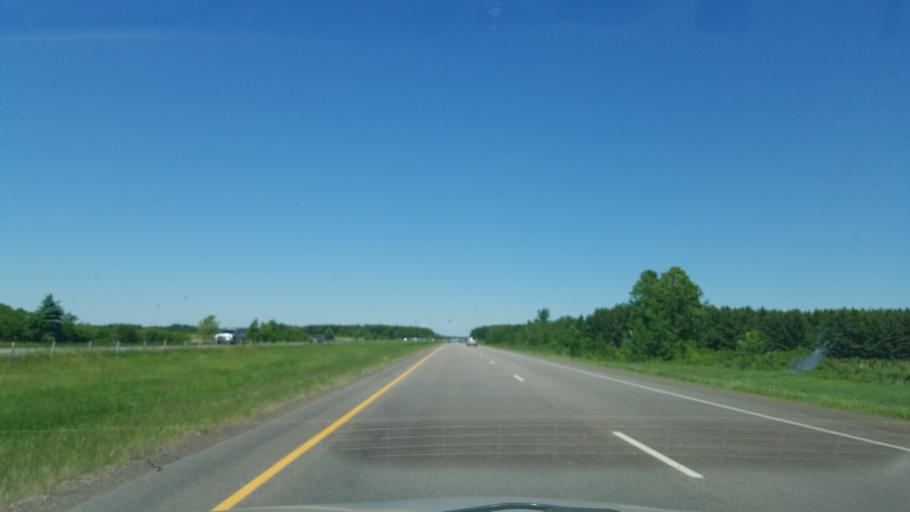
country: US
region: Minnesota
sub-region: Chisago County
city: Rush City
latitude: 45.7065
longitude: -92.9922
